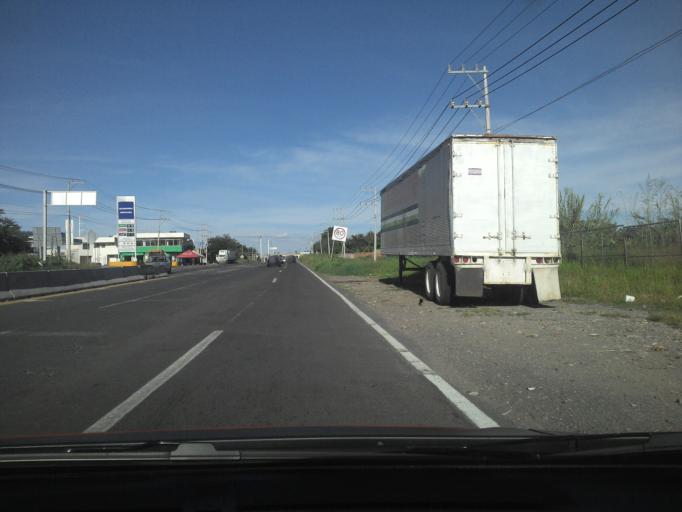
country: MX
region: Jalisco
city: El Refugio
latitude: 20.6675
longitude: -103.7181
